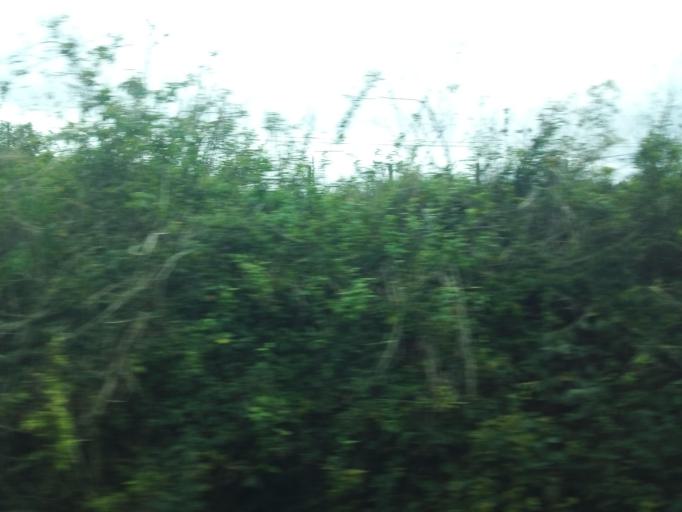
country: BR
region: Minas Gerais
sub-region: Ipatinga
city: Ipatinga
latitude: -19.4649
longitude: -42.4754
